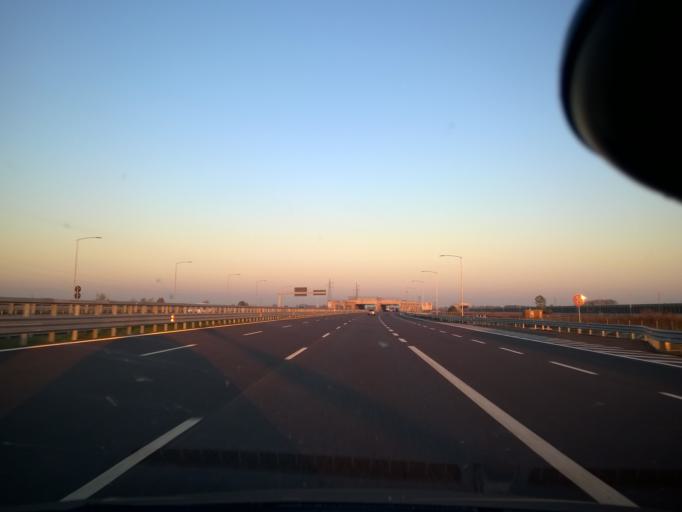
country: IT
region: Lombardy
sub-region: Provincia di Bergamo
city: Vidalengo
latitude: 45.5113
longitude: 9.6415
